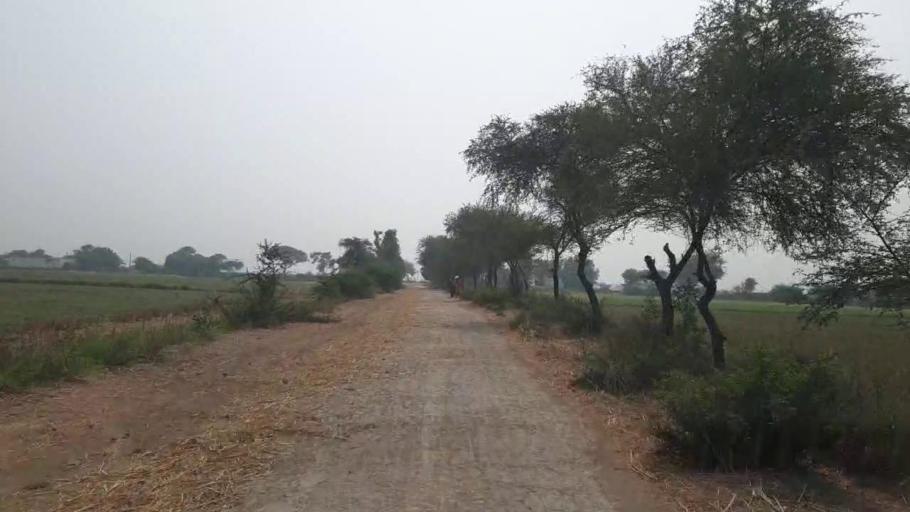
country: PK
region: Sindh
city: Kario
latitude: 24.6457
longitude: 68.6218
